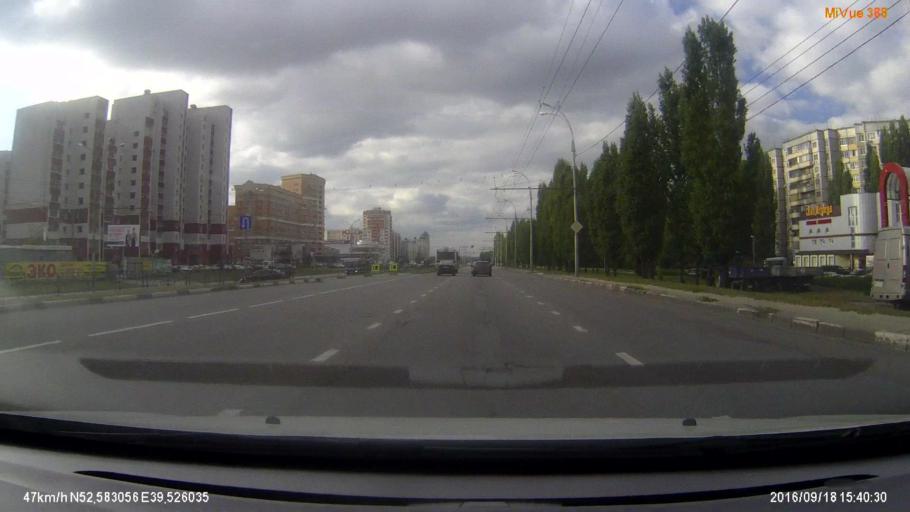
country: RU
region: Lipetsk
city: Syrskoye
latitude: 52.5834
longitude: 39.5255
